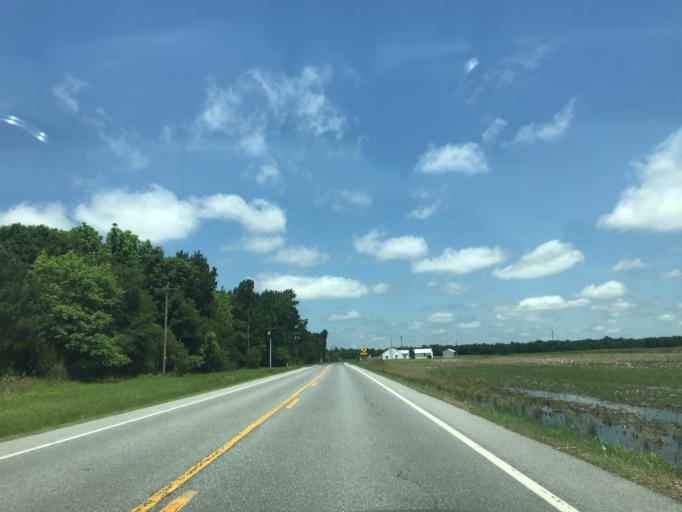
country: US
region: Maryland
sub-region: Caroline County
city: Federalsburg
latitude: 38.7221
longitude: -75.7354
